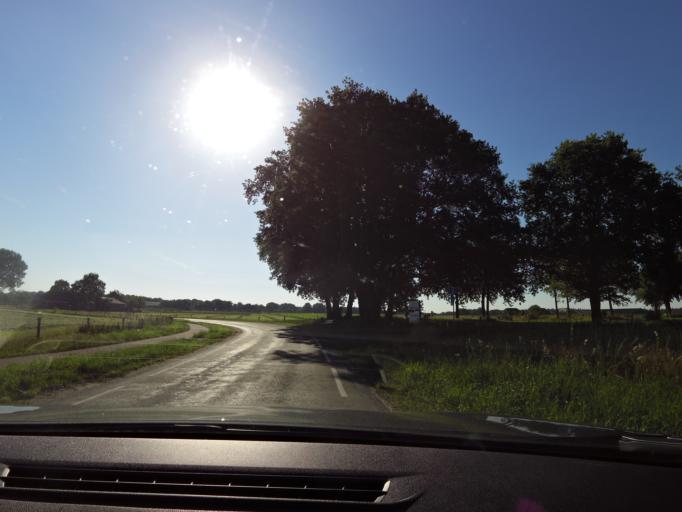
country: NL
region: Overijssel
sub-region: Gemeente Deventer
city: Schalkhaar
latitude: 52.2736
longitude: 6.2630
